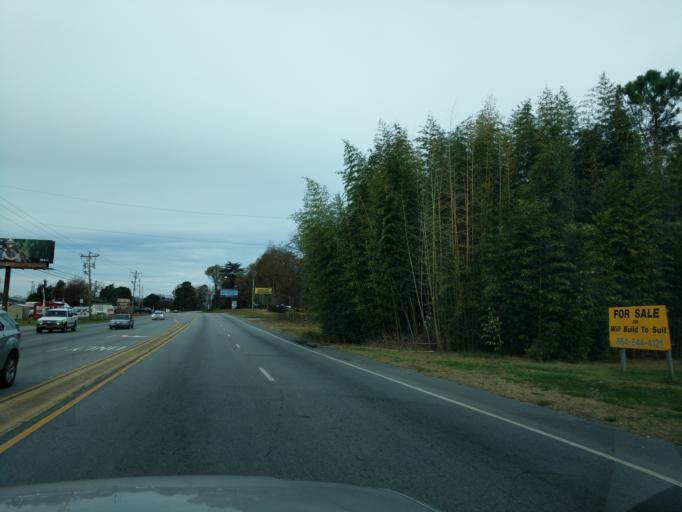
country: US
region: South Carolina
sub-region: Anderson County
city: Pendleton
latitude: 34.5947
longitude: -82.7491
